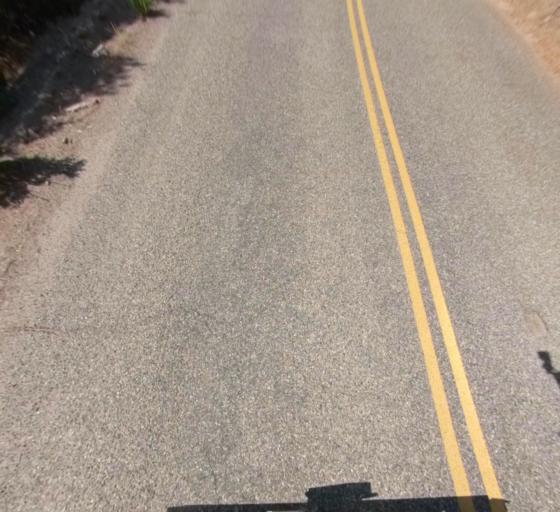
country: US
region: California
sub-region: Fresno County
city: Auberry
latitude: 37.2260
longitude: -119.3560
